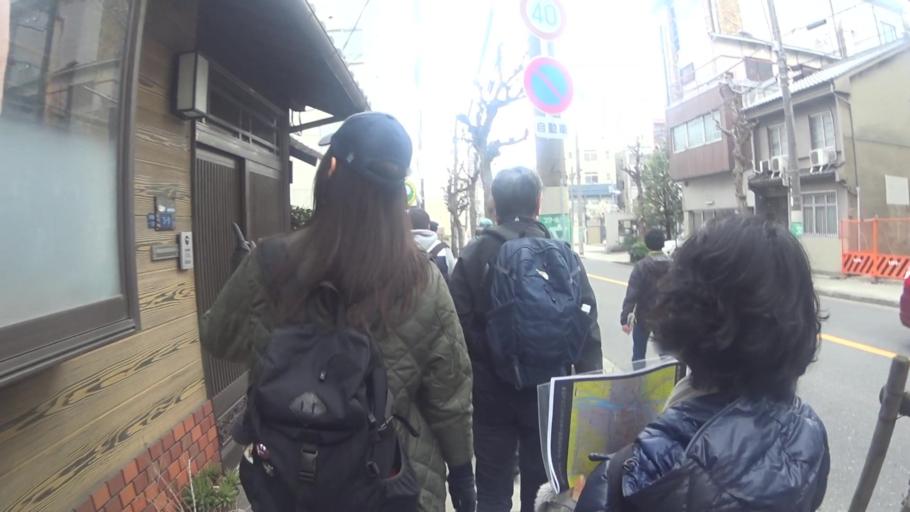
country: JP
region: Osaka
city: Osaka-shi
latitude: 34.6784
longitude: 135.5259
